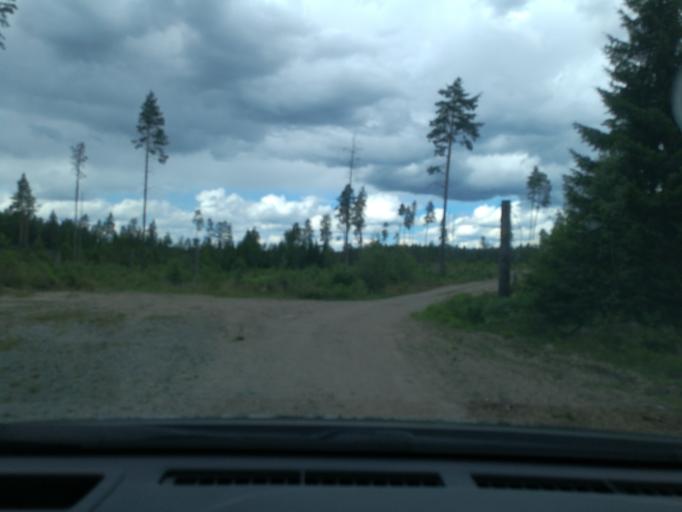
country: SE
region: Vaestmanland
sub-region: Vasteras
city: Skultuna
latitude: 59.7934
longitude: 16.3320
